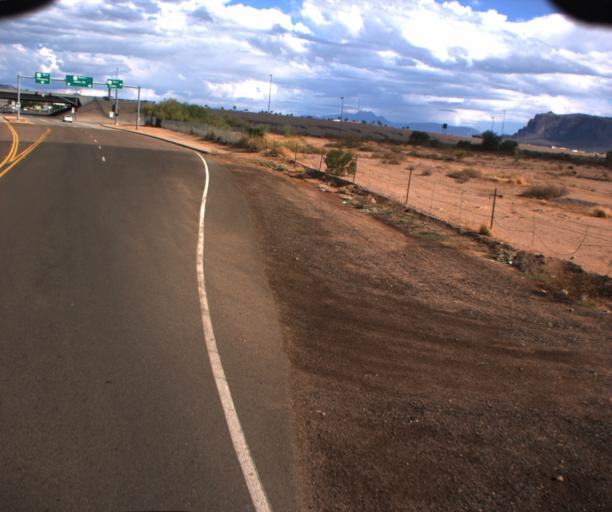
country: US
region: Arizona
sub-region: Pinal County
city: Apache Junction
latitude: 33.3844
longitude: -111.5461
